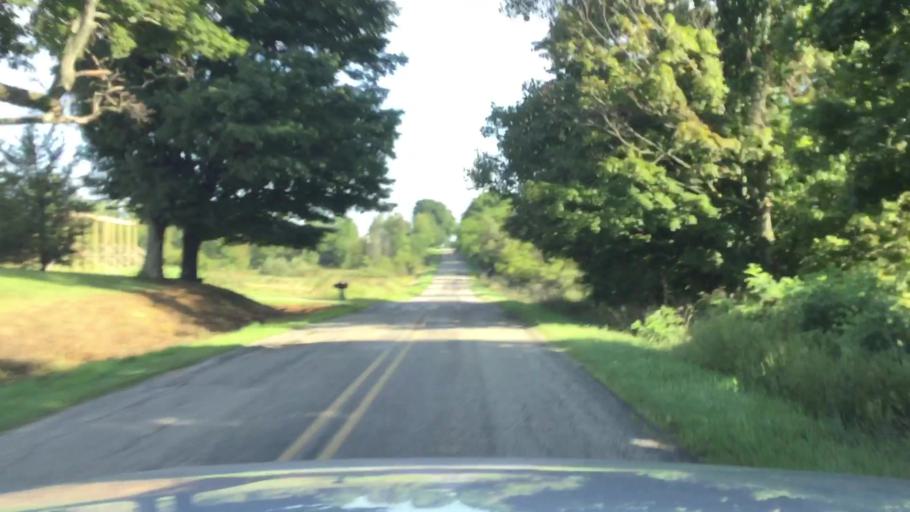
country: US
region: Michigan
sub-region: Lenawee County
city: Hudson
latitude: 41.8921
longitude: -84.4203
